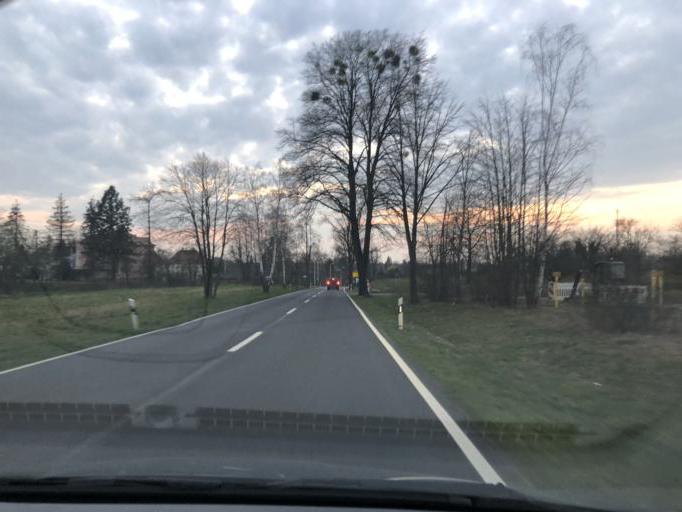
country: DE
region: Saxony
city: Konigsbruck
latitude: 51.2629
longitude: 13.9199
